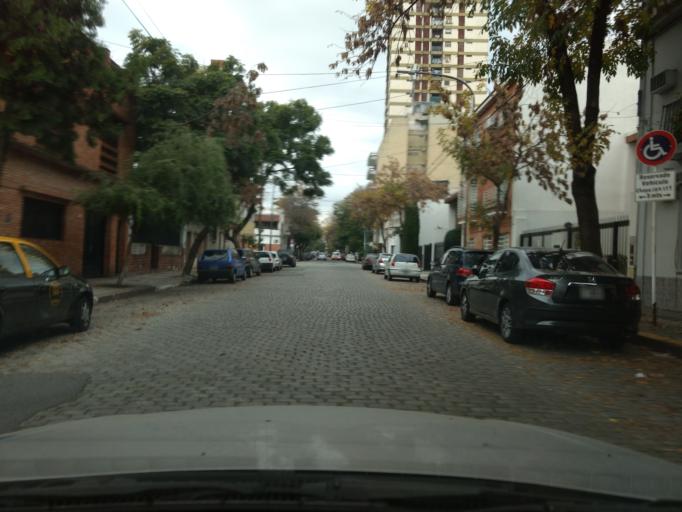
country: AR
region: Buenos Aires F.D.
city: Villa Santa Rita
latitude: -34.6196
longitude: -58.4675
